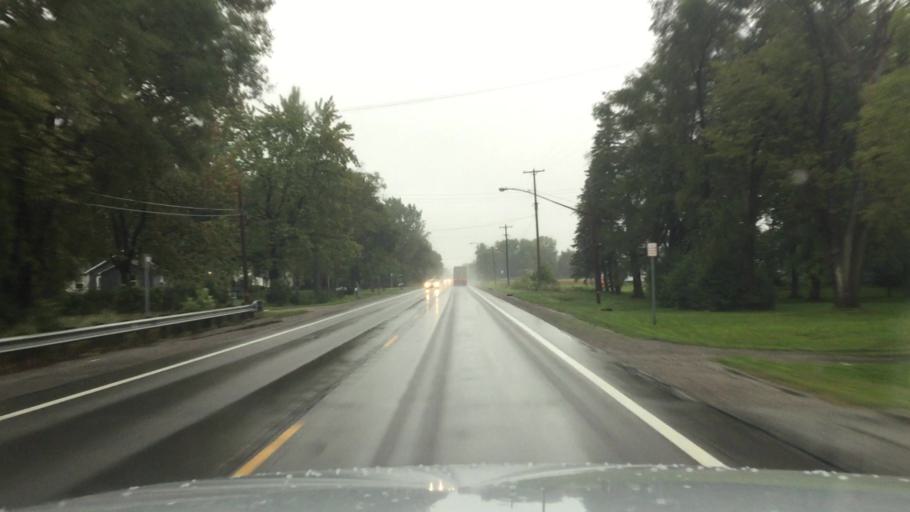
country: US
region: Michigan
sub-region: Saginaw County
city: Saginaw
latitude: 43.3847
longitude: -83.9554
